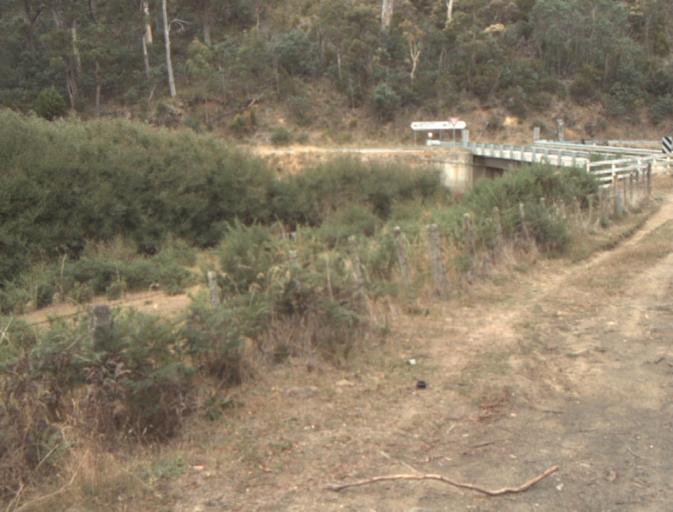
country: AU
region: Tasmania
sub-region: Northern Midlands
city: Evandale
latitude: -41.4926
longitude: 147.4323
